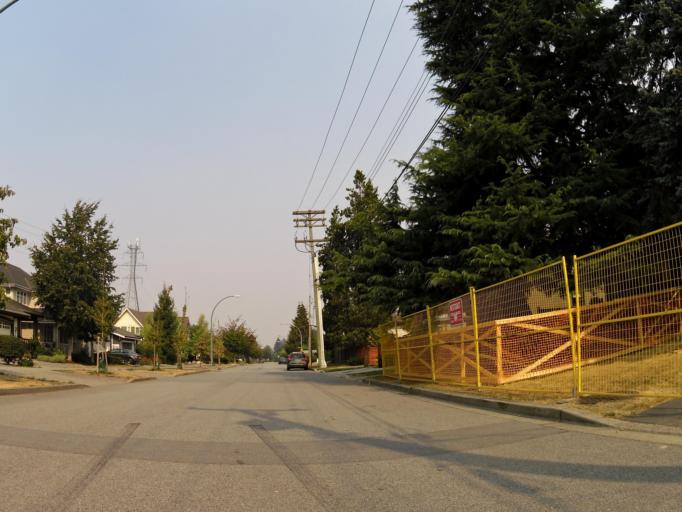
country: CA
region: British Columbia
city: Delta
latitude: 49.1533
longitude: -122.9234
